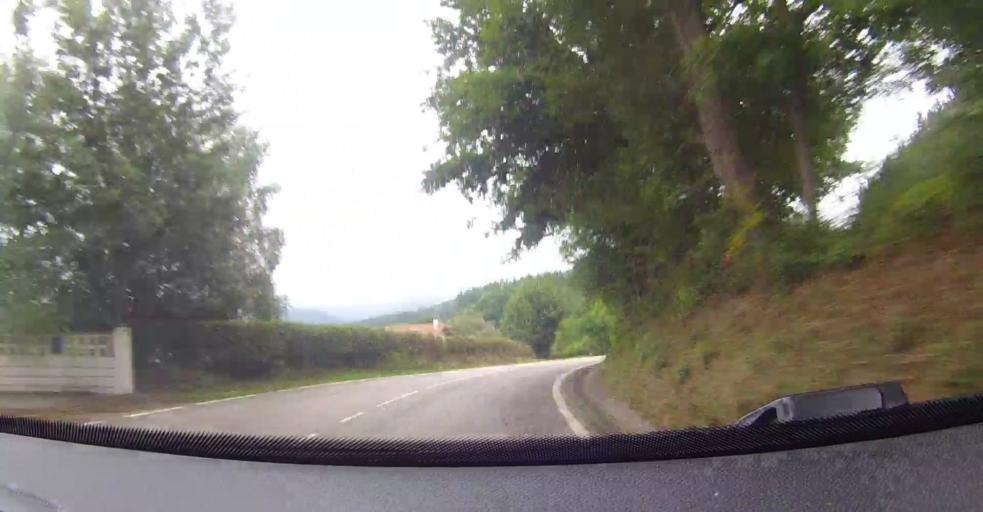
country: ES
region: Basque Country
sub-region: Bizkaia
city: Balmaseda
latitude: 43.2502
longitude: -3.2749
